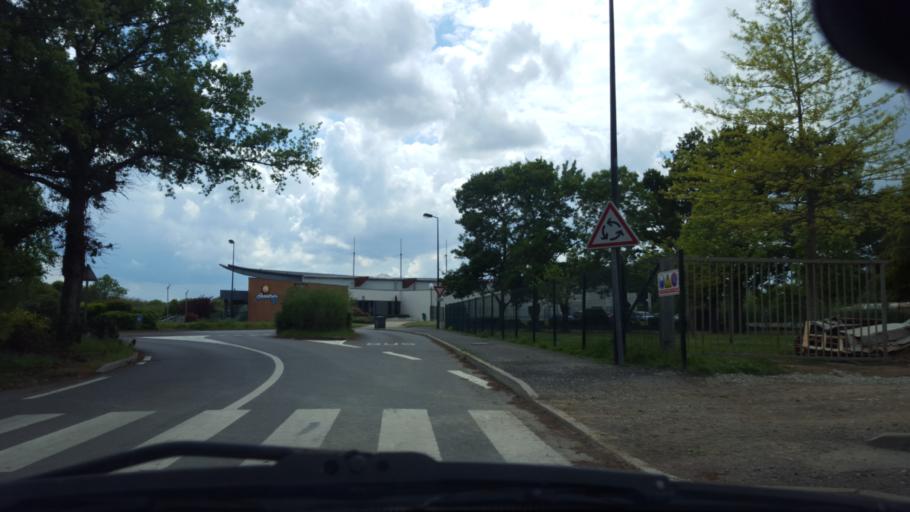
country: FR
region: Pays de la Loire
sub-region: Departement de la Loire-Atlantique
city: Saint-Philbert-de-Grand-Lieu
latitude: 47.0451
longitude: -1.6360
